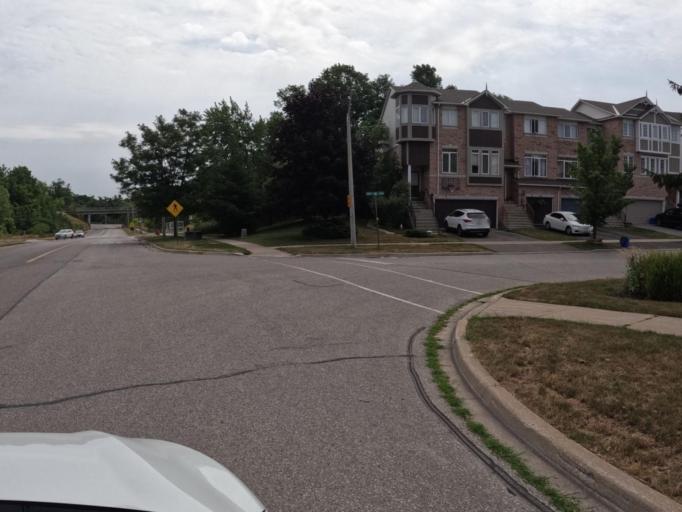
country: CA
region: Ontario
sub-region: Halton
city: Milton
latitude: 43.6432
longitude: -79.9380
